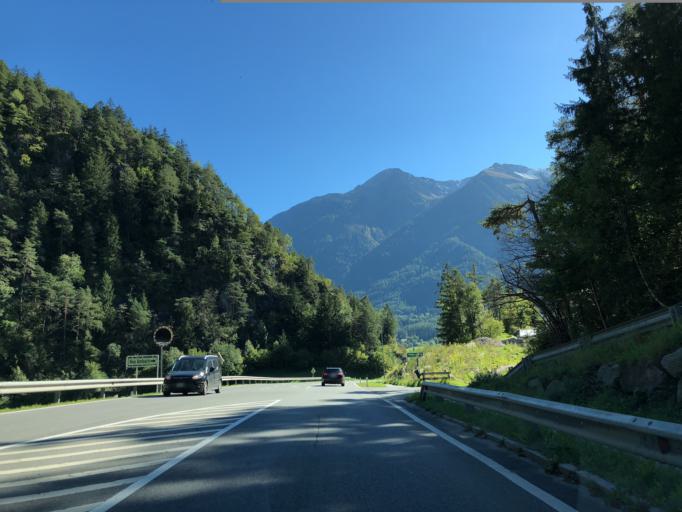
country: AT
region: Tyrol
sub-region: Politischer Bezirk Imst
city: Sautens
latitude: 47.2179
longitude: 10.8666
